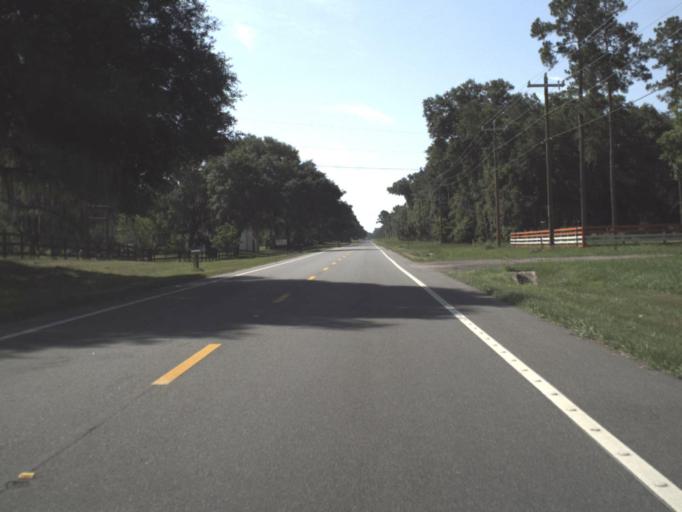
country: US
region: Florida
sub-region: Madison County
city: Madison
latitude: 30.4283
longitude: -83.3854
